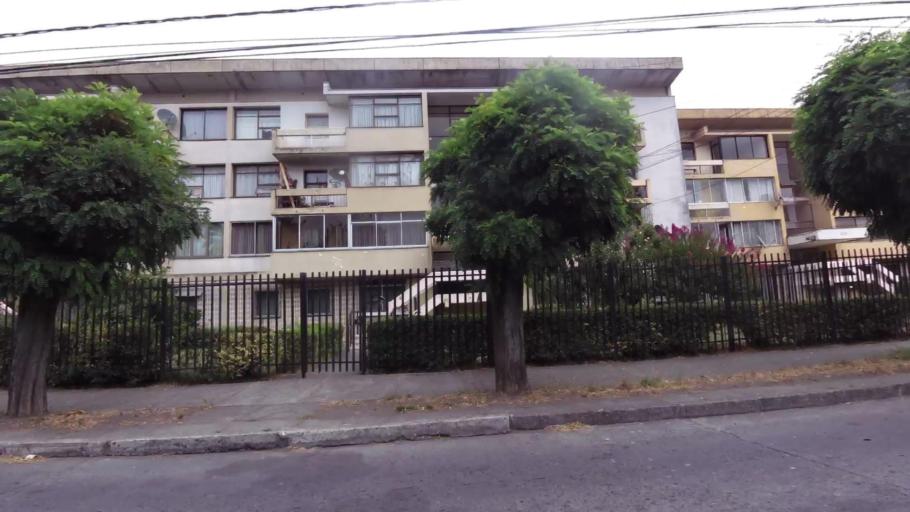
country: CL
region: Biobio
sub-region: Provincia de Concepcion
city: Concepcion
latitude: -36.8175
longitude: -73.0443
